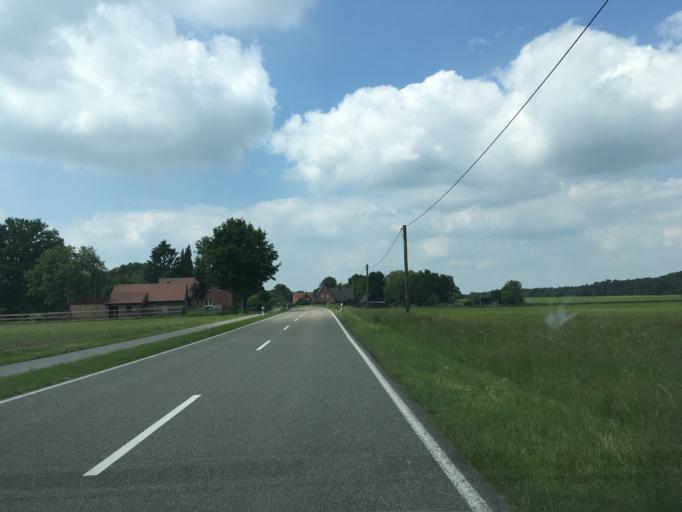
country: DE
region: North Rhine-Westphalia
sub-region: Regierungsbezirk Munster
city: Rhede
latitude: 51.7900
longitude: 6.7657
